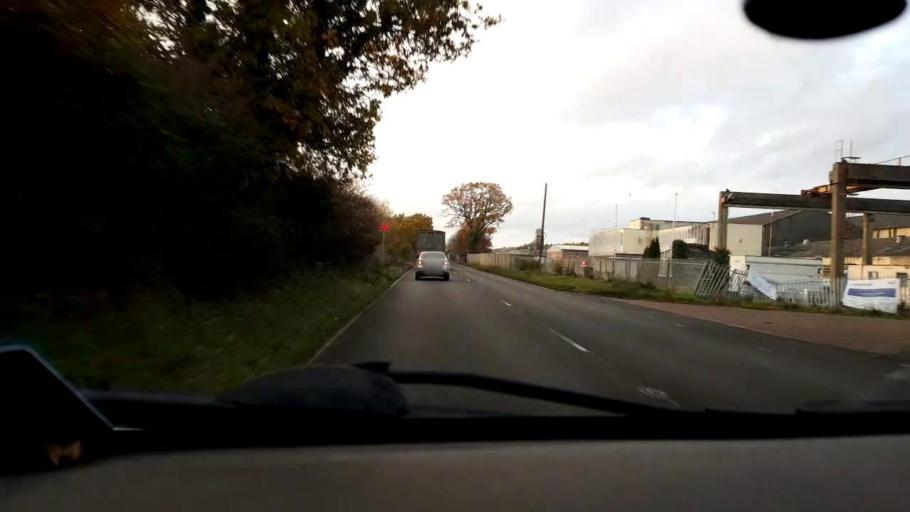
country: GB
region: England
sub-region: Norfolk
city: Costessey
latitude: 52.7140
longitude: 1.1334
